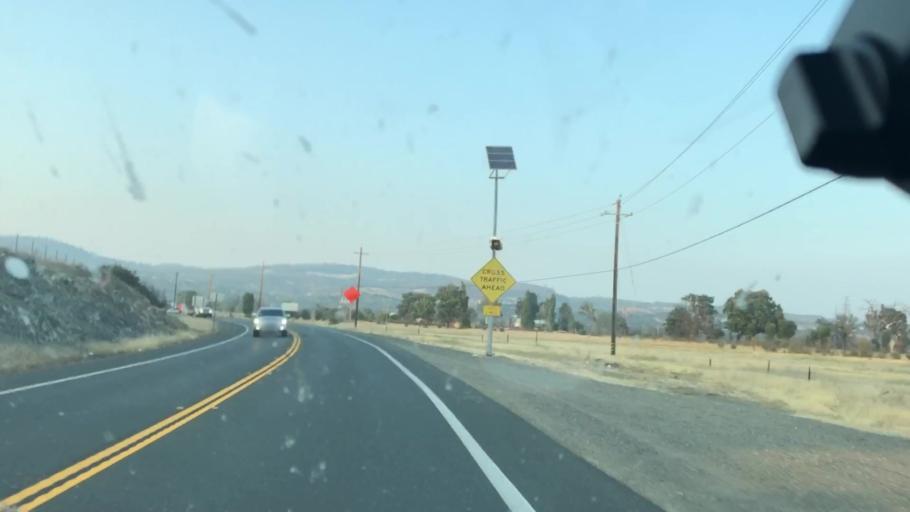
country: US
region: California
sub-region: Lake County
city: Hidden Valley Lake
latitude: 38.7814
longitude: -122.5701
